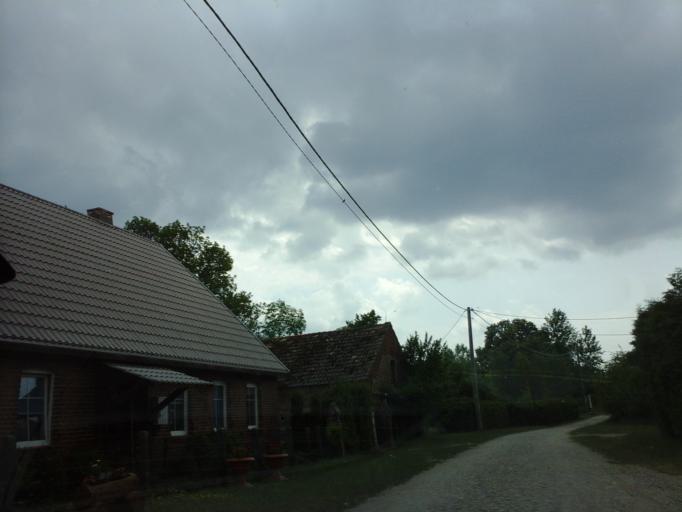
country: PL
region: West Pomeranian Voivodeship
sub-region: Powiat walecki
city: Miroslawiec
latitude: 53.2518
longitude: 16.0209
